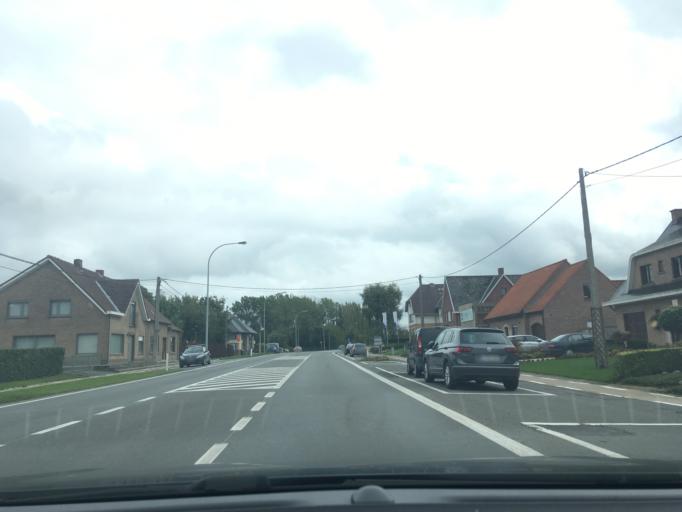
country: BE
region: Flanders
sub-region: Provincie West-Vlaanderen
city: Zonnebeke
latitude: 50.8453
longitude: 2.9541
